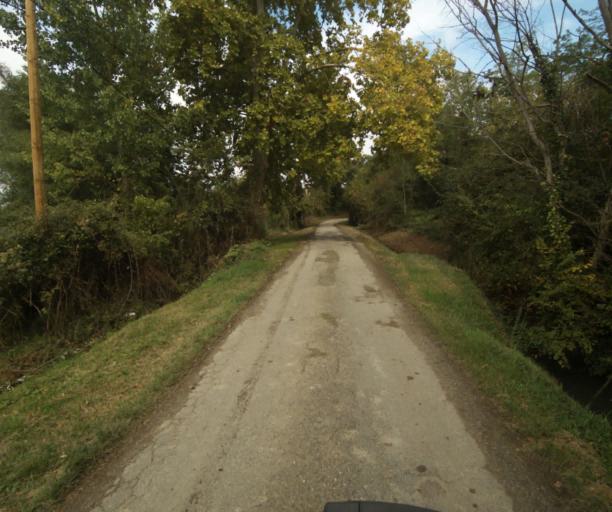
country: FR
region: Midi-Pyrenees
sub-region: Departement du Tarn-et-Garonne
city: Montech
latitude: 43.9424
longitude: 1.2100
